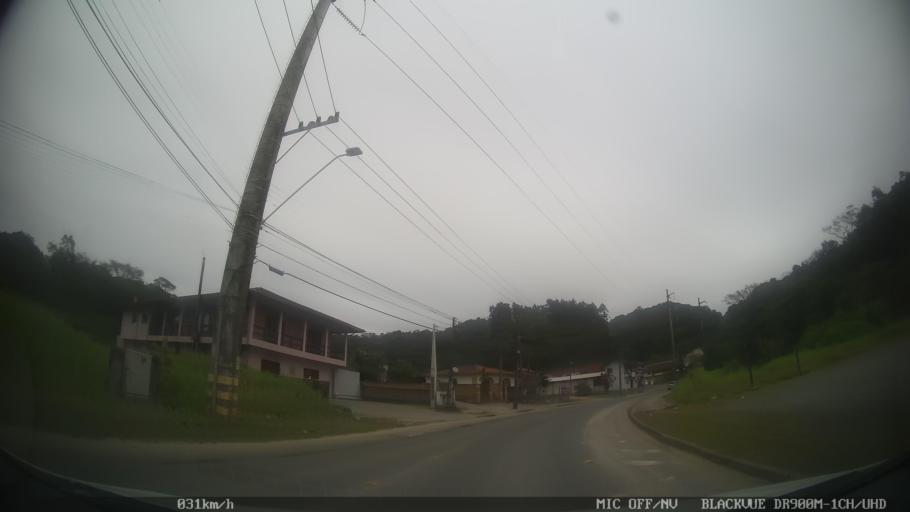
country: BR
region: Santa Catarina
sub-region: Joinville
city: Joinville
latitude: -26.3566
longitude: -48.7958
